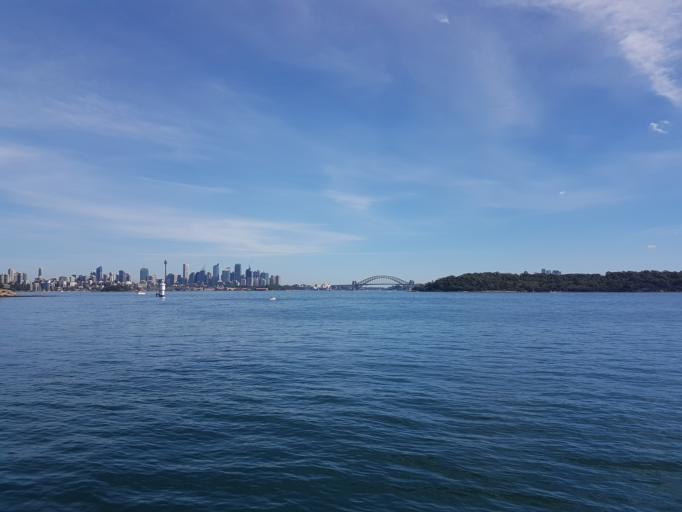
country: AU
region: New South Wales
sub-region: Woollahra
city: Point Piper
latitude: -33.8552
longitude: 151.2619
